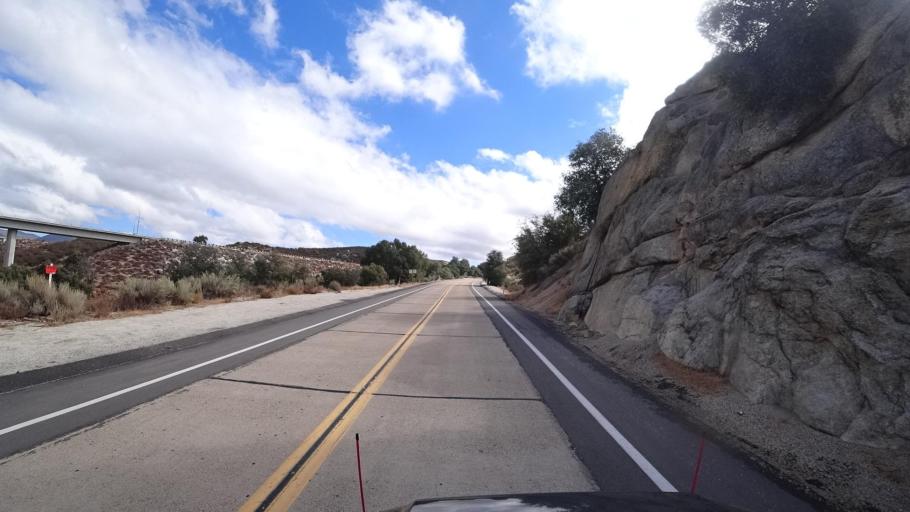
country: US
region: California
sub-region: San Diego County
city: Campo
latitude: 32.7250
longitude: -116.4262
